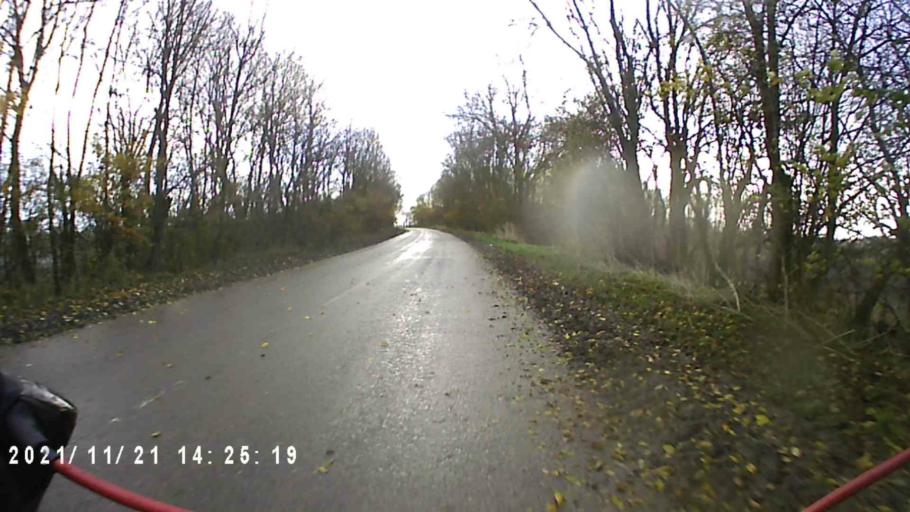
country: NL
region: Groningen
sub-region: Gemeente De Marne
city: Ulrum
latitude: 53.3677
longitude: 6.2935
